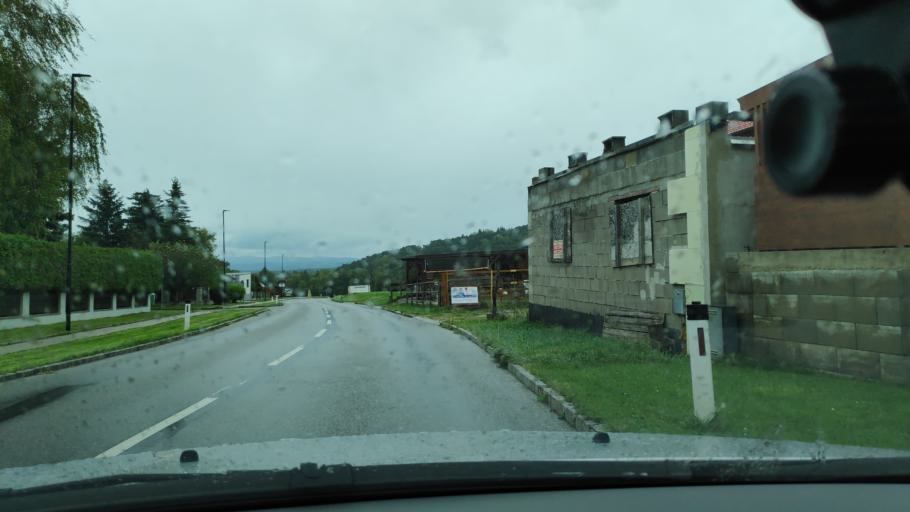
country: AT
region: Lower Austria
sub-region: Politischer Bezirk Neunkirchen
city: Willendorf am Steinfelde
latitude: 47.7935
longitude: 16.0392
